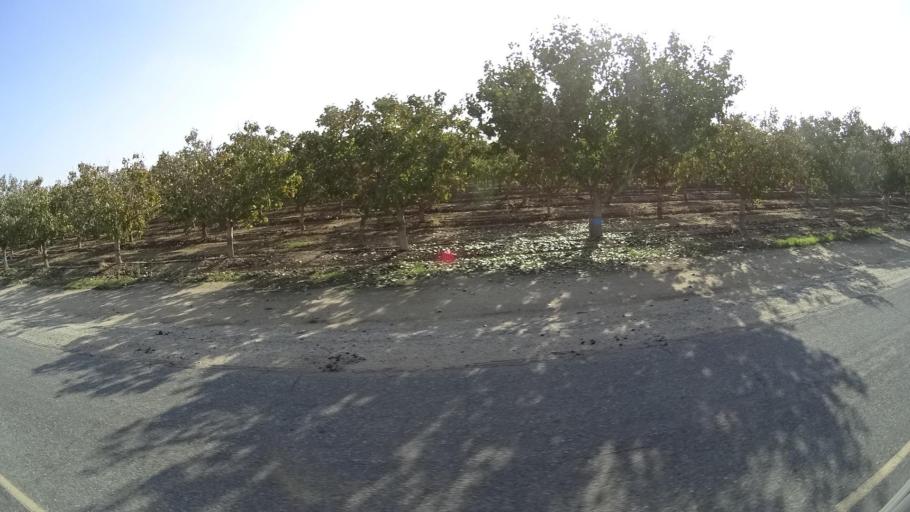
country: US
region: California
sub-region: Tulare County
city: Richgrove
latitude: 35.7908
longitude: -119.0949
